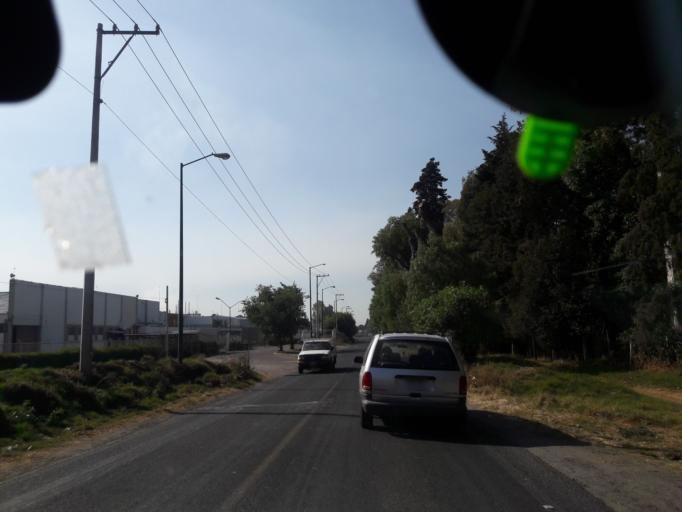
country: MX
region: Tlaxcala
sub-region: Ixtacuixtla de Mariano Matamoros
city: Villa Mariano Matamoros
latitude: 19.3141
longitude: -98.3870
